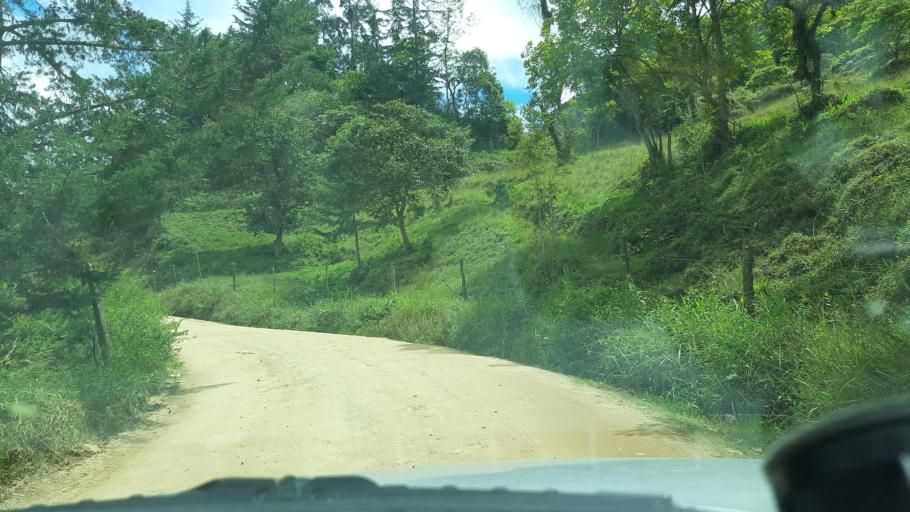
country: CO
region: Cundinamarca
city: Umbita
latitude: 5.2210
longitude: -73.4297
